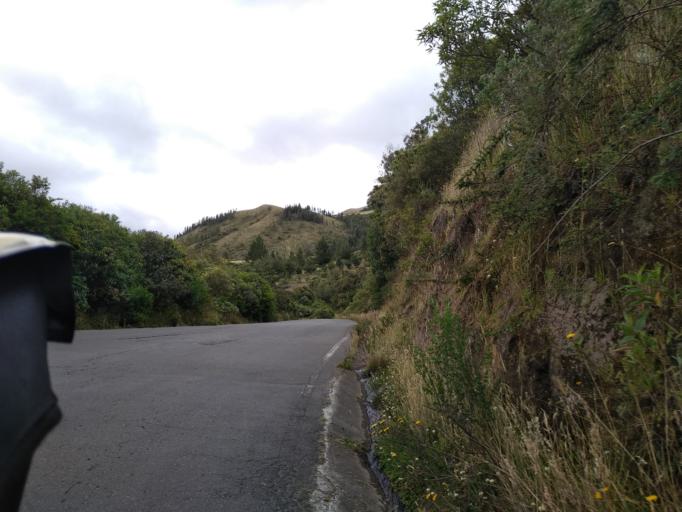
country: EC
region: Cotopaxi
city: Saquisili
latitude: -0.7142
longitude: -78.7638
